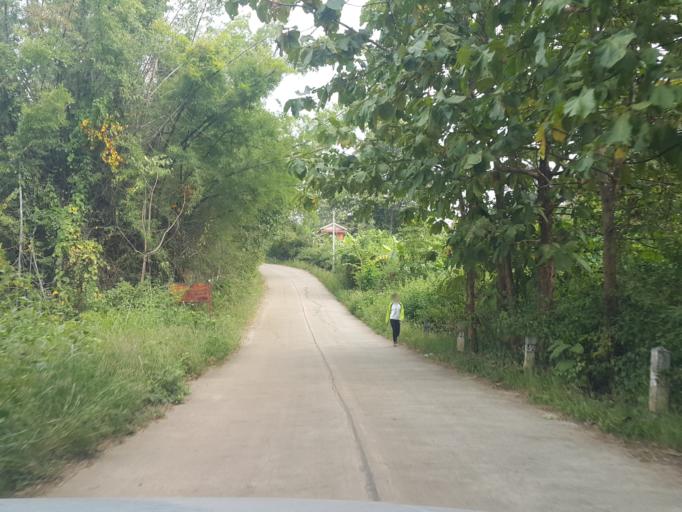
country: TH
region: Chiang Mai
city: Pai
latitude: 19.3676
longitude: 98.4499
